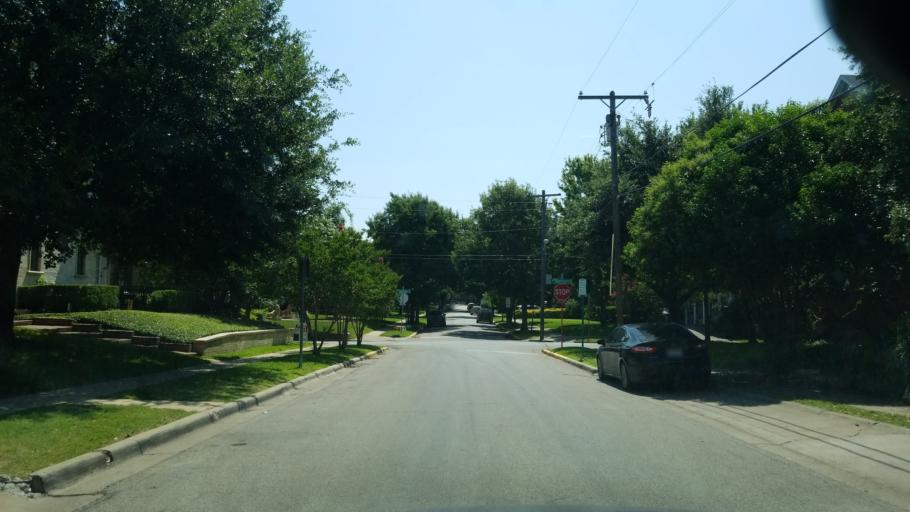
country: US
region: Texas
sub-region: Dallas County
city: Highland Park
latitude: 32.8479
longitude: -96.7814
